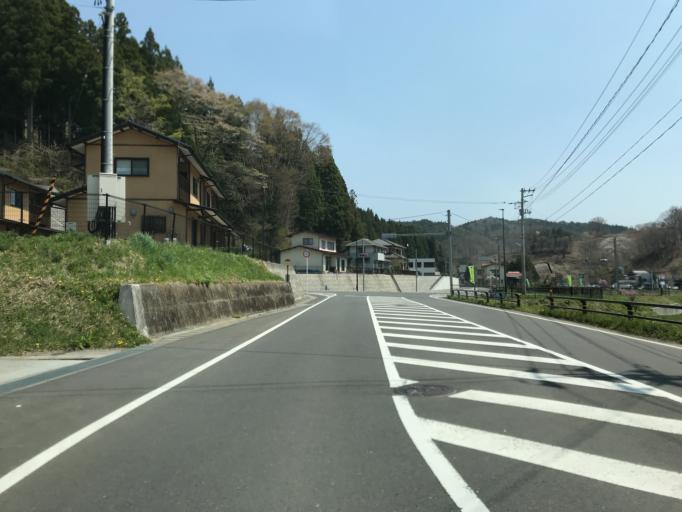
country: JP
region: Fukushima
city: Ishikawa
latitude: 37.0460
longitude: 140.5014
